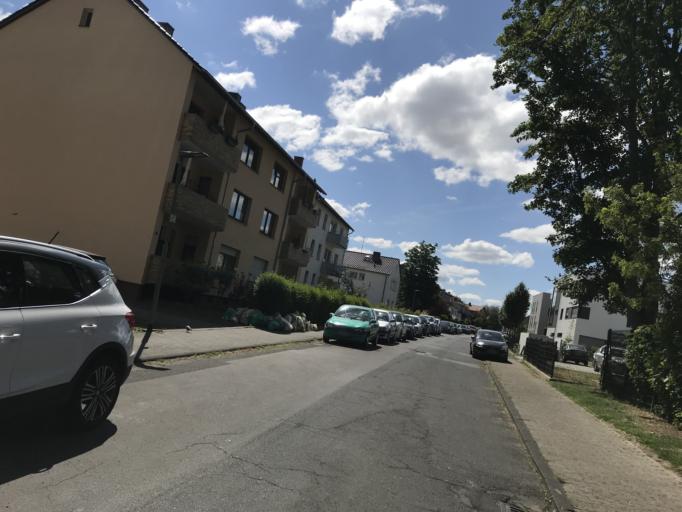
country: DE
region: Hesse
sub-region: Regierungsbezirk Darmstadt
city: Friedberg
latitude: 50.3280
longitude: 8.7573
